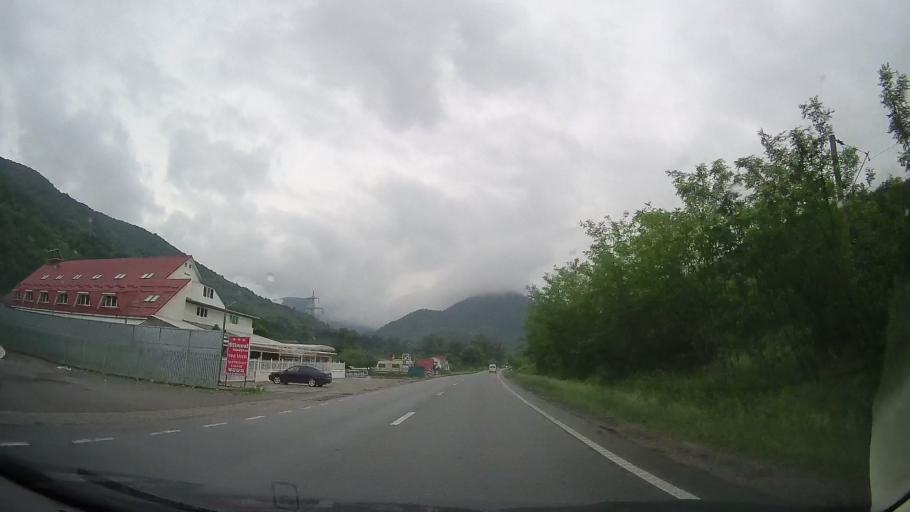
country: RO
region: Caras-Severin
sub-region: Oras Baile Herculane
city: Baile Herculane
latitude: 44.8695
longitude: 22.3875
